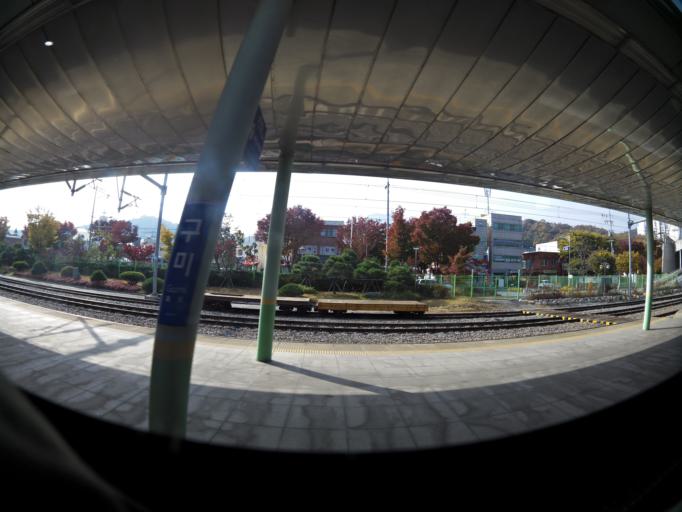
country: KR
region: Gyeongsangbuk-do
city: Gumi
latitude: 36.1276
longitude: 128.3325
